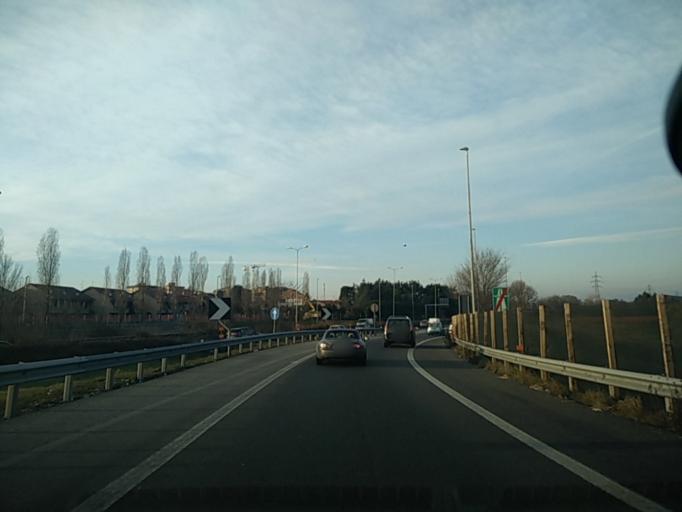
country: IT
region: Lombardy
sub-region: Citta metropolitana di Milano
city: Cusano Milanino
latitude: 45.5632
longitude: 9.1783
